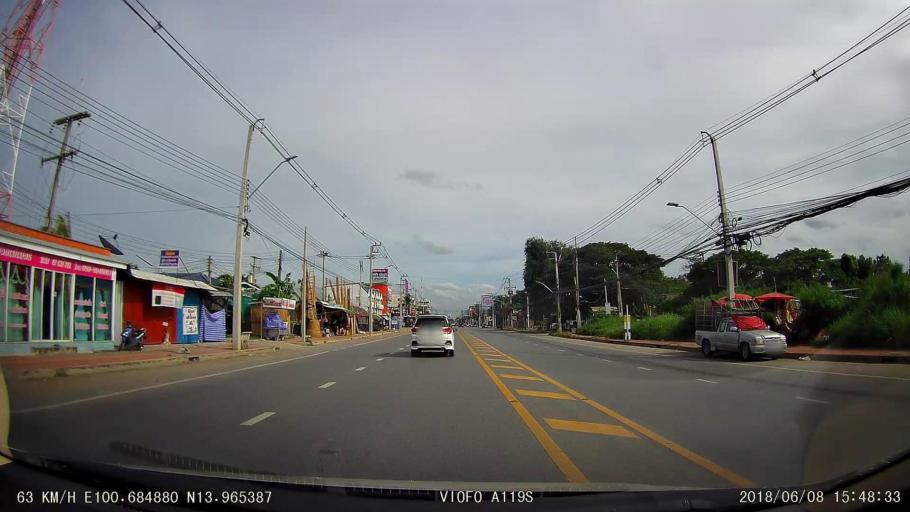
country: TH
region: Bangkok
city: Sai Mai
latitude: 13.9652
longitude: 100.6849
